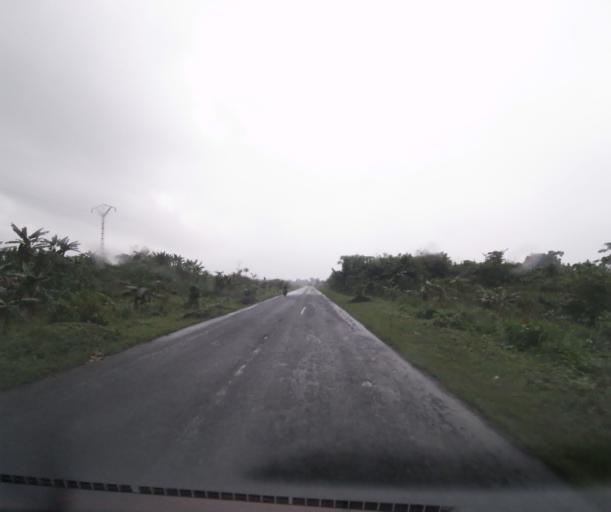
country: CM
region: South-West Province
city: Idenao
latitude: 4.1766
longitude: 8.9998
